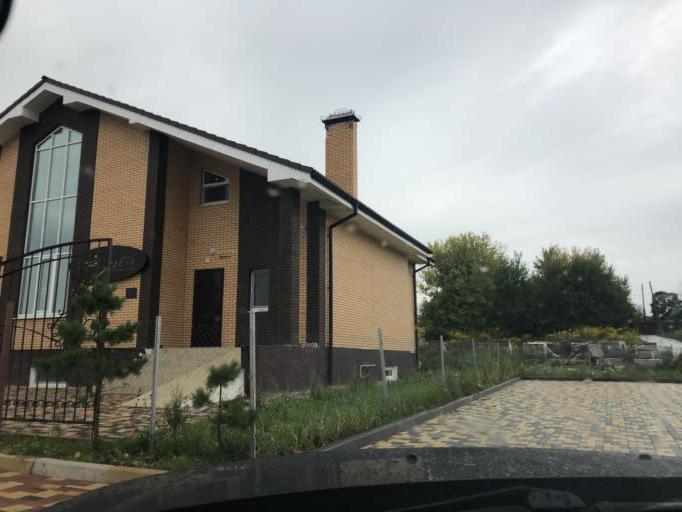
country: RU
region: Tula
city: Barsuki
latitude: 54.1982
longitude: 37.5161
